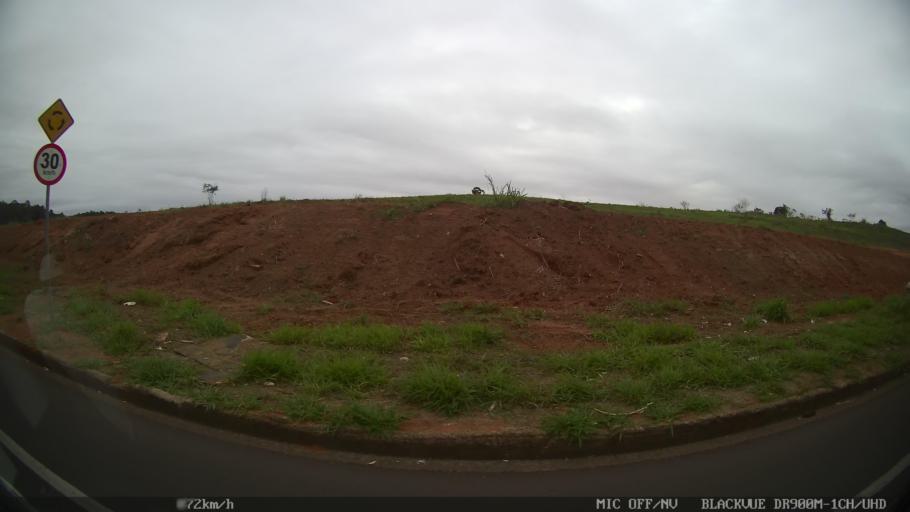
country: BR
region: Sao Paulo
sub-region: Sao Jose Do Rio Preto
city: Sao Jose do Rio Preto
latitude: -20.8245
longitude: -49.4350
